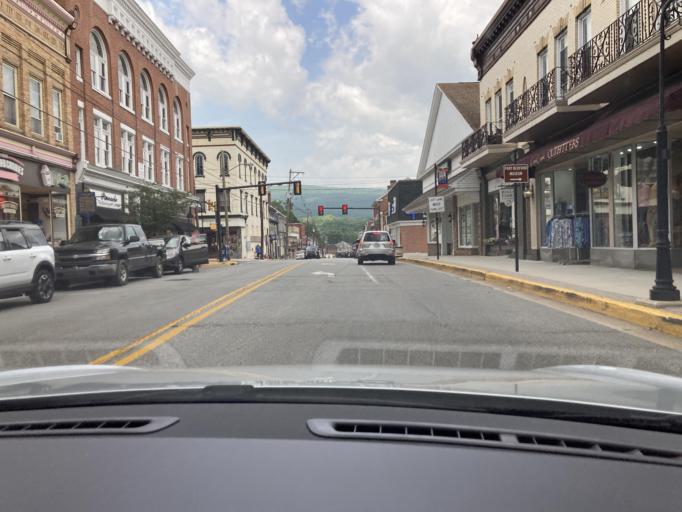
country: US
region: Pennsylvania
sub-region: Bedford County
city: Bedford
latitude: 40.0191
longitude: -78.5033
